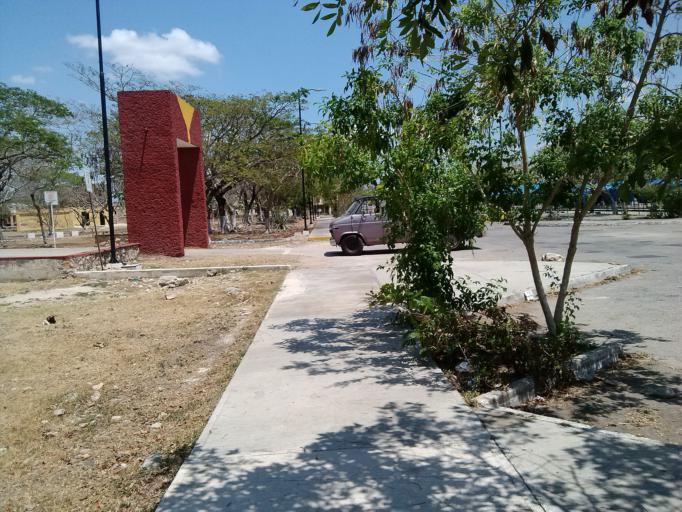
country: MX
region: Yucatan
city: Merida
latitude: 20.9687
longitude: -89.5832
